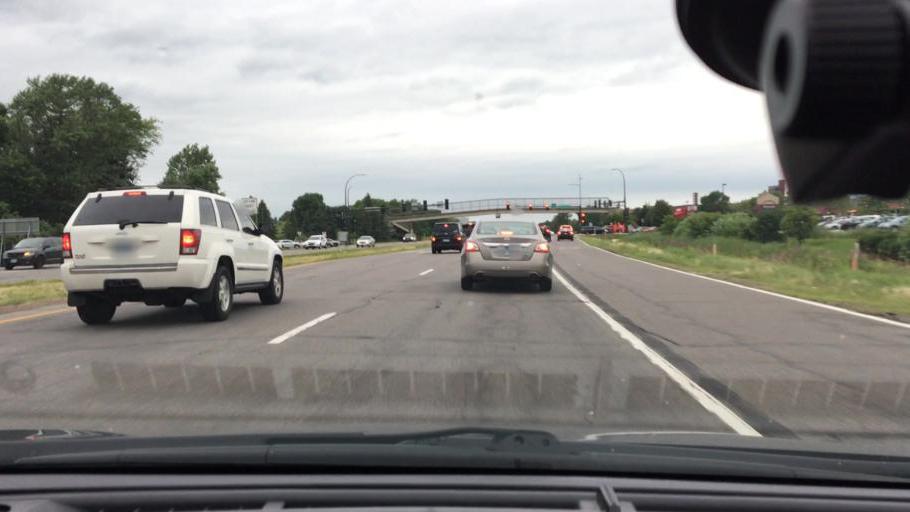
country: US
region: Minnesota
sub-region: Hennepin County
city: Golden Valley
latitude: 44.9835
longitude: -93.3783
